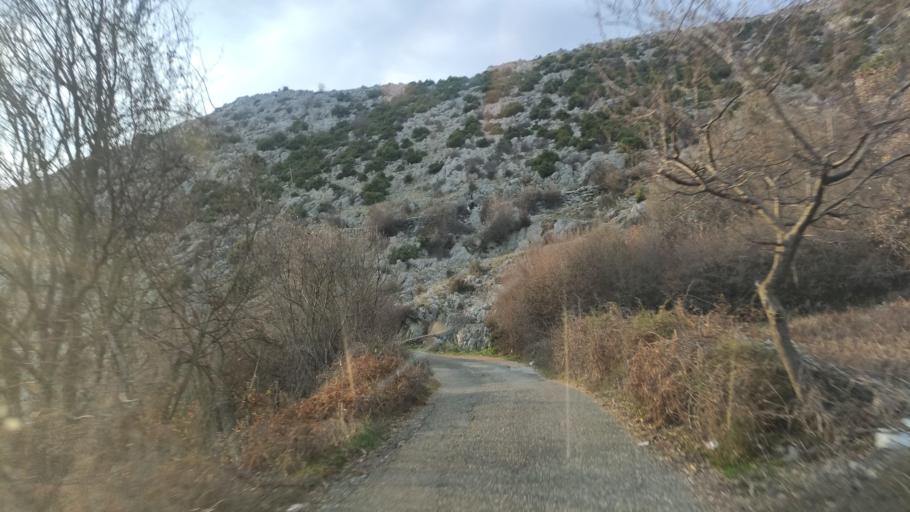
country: AL
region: Shkoder
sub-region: Rrethi i Malesia e Madhe
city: Gruemire
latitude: 42.2405
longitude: 19.5362
